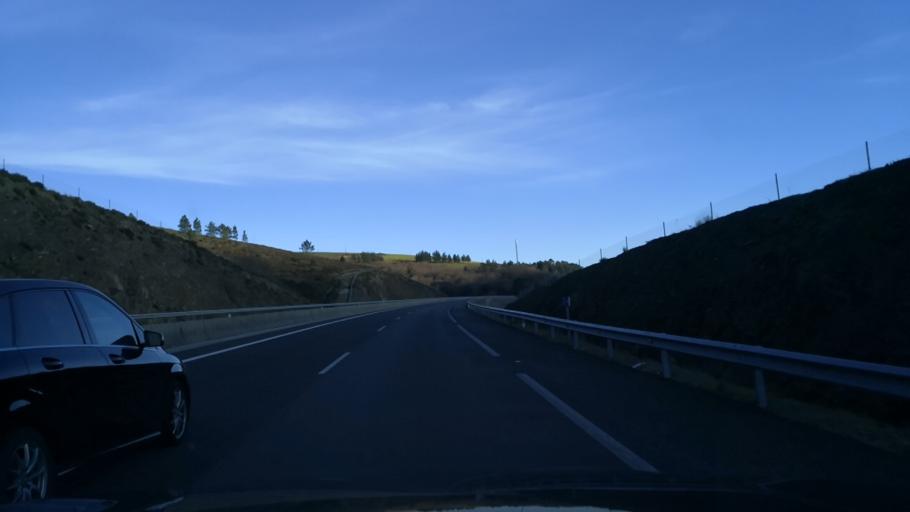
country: ES
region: Galicia
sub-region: Provincia de Pontevedra
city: Lalin
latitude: 42.5987
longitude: -8.0900
